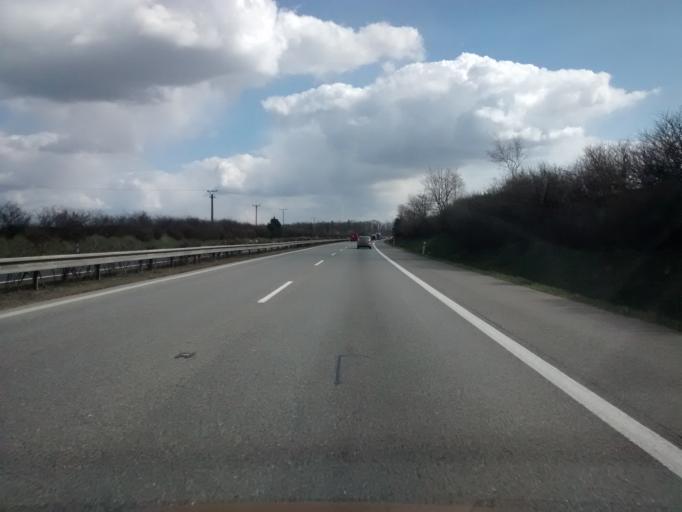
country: CZ
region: Central Bohemia
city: Odolena Voda
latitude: 50.2176
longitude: 14.4227
